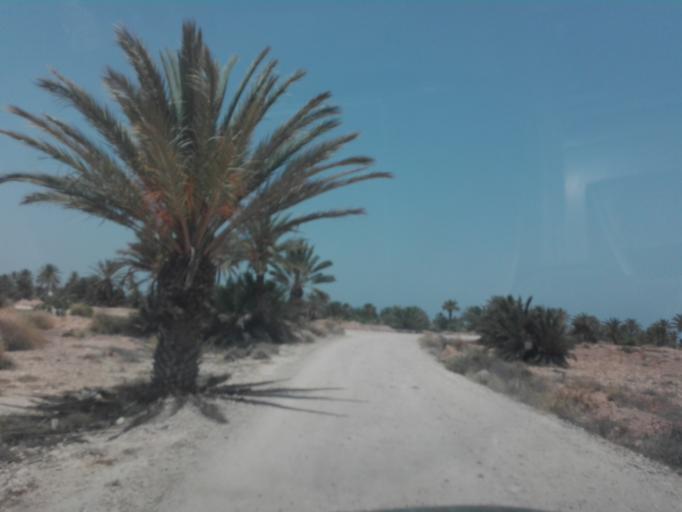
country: TN
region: Safaqis
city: Al Qarmadah
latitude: 34.6625
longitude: 11.0929
